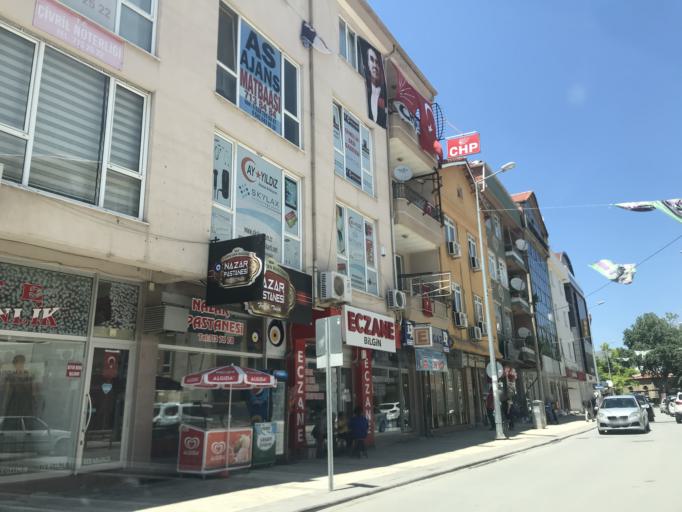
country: TR
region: Denizli
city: Civril
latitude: 38.2997
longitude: 29.7400
